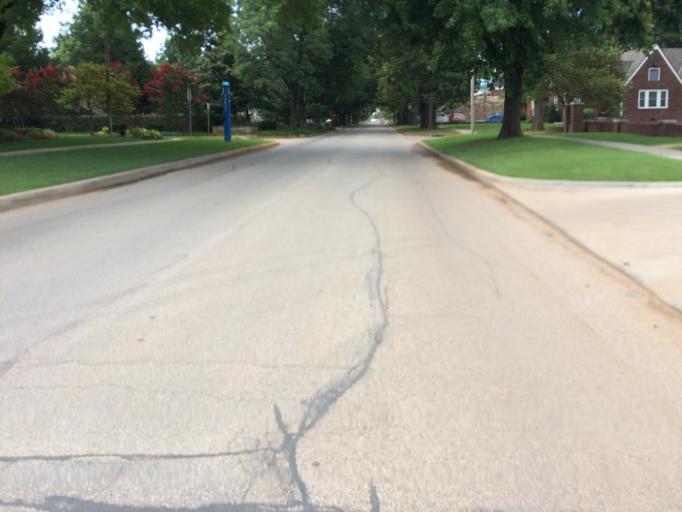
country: US
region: Oklahoma
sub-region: Cleveland County
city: Norman
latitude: 35.2061
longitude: -97.4502
